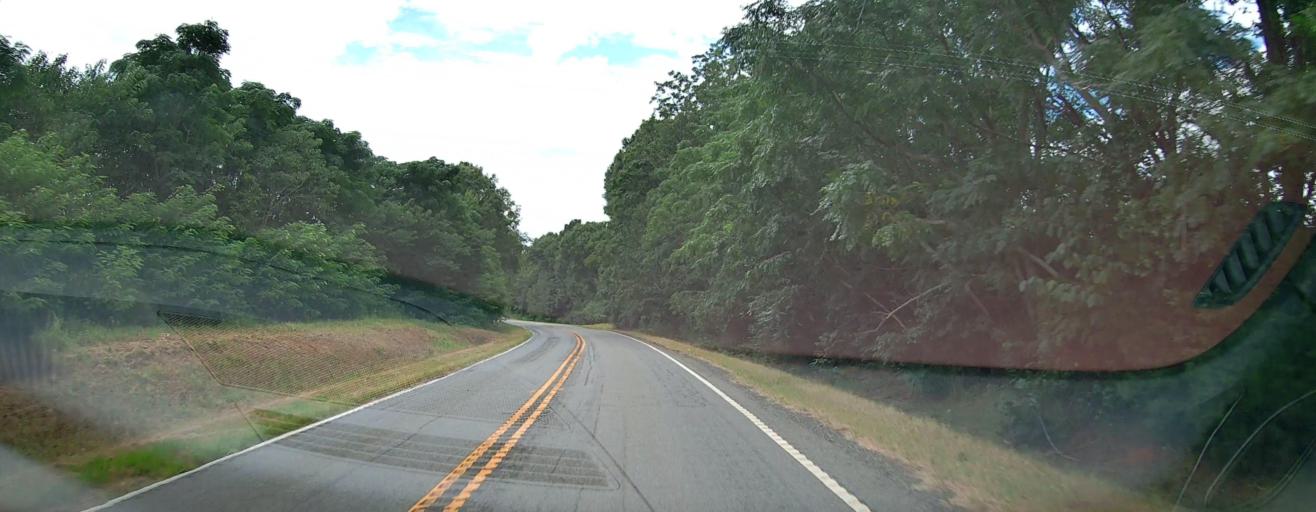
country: US
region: Georgia
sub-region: Macon County
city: Montezuma
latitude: 32.2947
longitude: -83.9043
